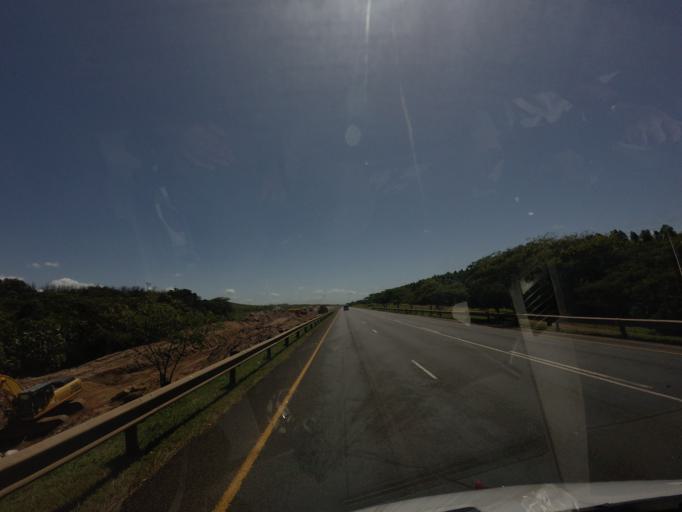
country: ZA
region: KwaZulu-Natal
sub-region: uThungulu District Municipality
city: eSikhawini
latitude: -28.9222
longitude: 31.8000
